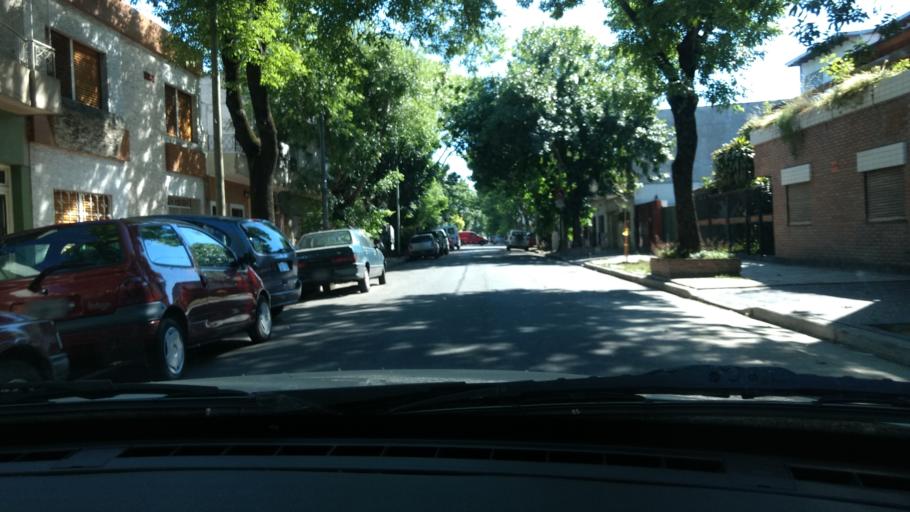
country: AR
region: Buenos Aires F.D.
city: Villa Santa Rita
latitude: -34.6114
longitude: -58.5118
